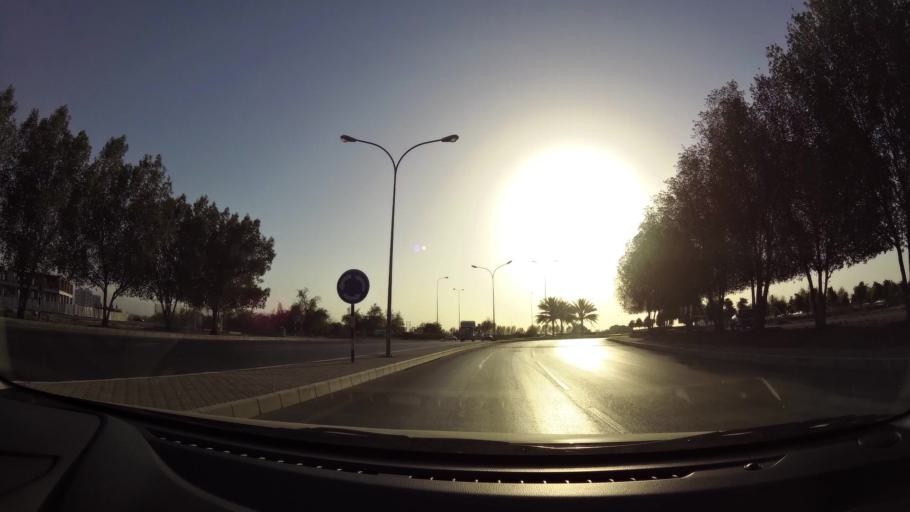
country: OM
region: Muhafazat Masqat
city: As Sib al Jadidah
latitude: 23.6180
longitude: 58.1812
